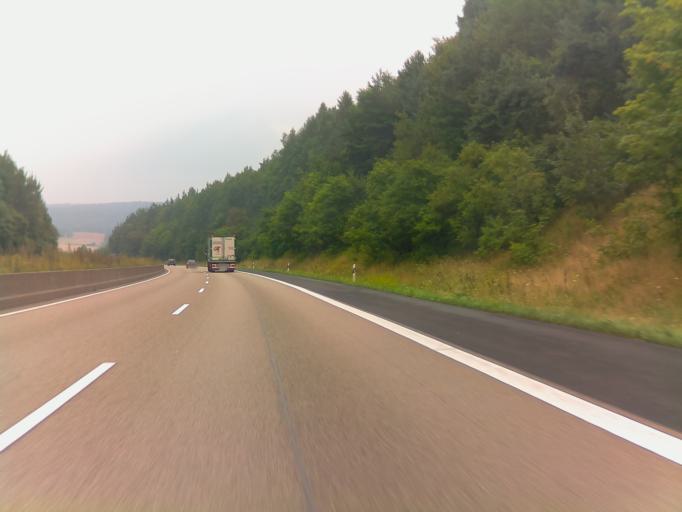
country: DE
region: Hesse
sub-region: Regierungsbezirk Kassel
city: Burghaun
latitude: 50.6447
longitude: 9.6830
